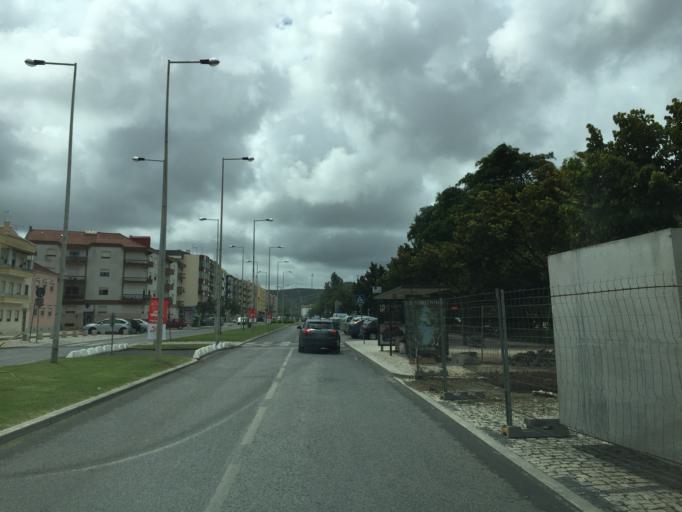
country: PT
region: Lisbon
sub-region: Torres Vedras
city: Torres Vedras
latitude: 39.0895
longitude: -9.2612
